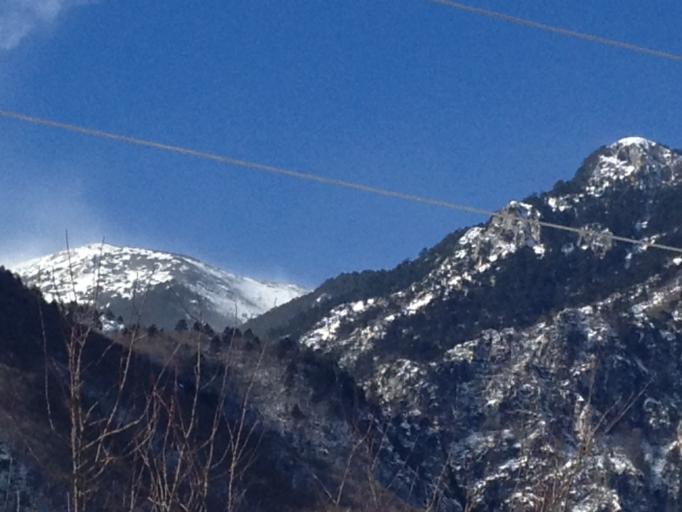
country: XK
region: Gjakova
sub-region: Komuna e Decanit
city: Strellc i Eperm
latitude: 42.5964
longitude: 20.2930
